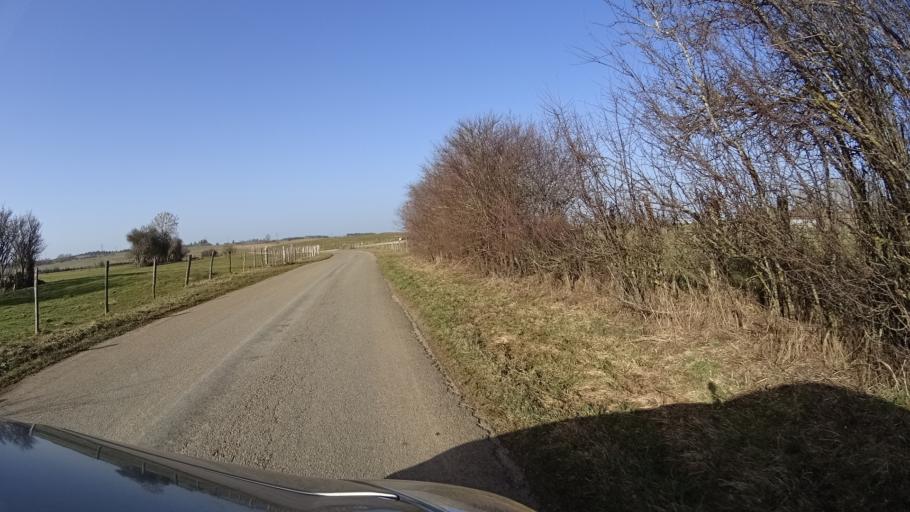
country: FR
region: Franche-Comte
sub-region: Departement du Doubs
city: Frasne
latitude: 46.8933
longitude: 6.2165
